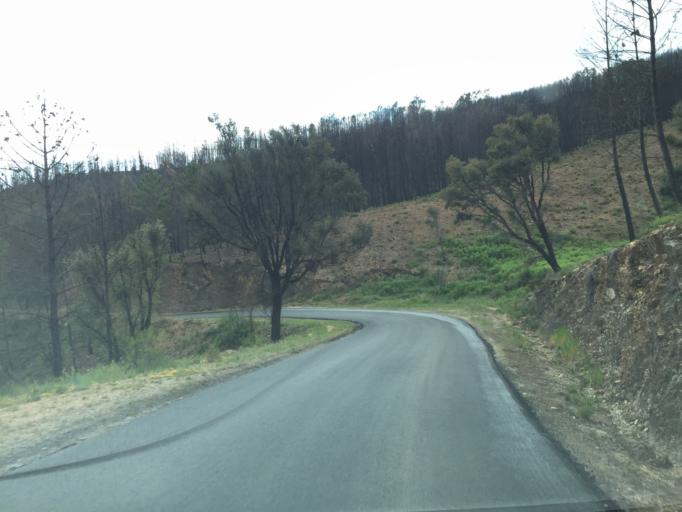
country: PT
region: Coimbra
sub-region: Pampilhosa da Serra
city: Pampilhosa da Serra
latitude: 40.0575
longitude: -8.0131
